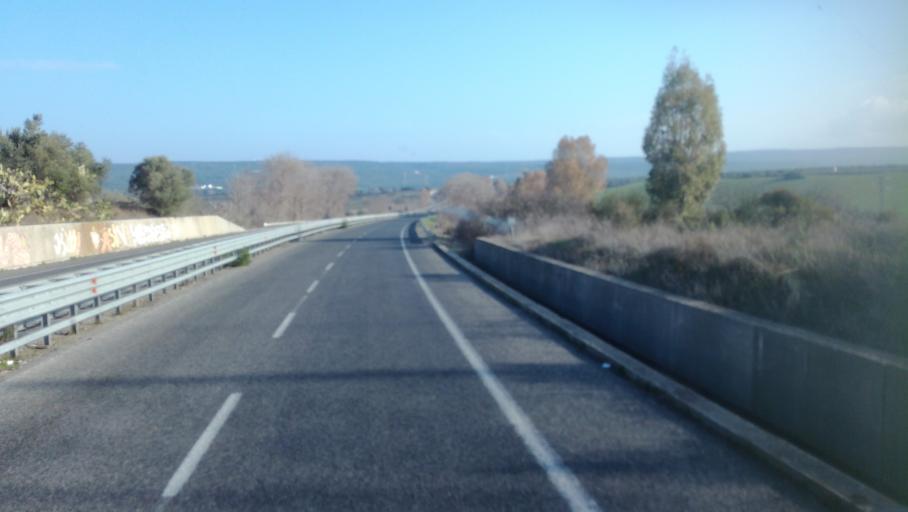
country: IT
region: Apulia
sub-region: Provincia di Taranto
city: Montemesola
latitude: 40.5969
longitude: 17.2914
